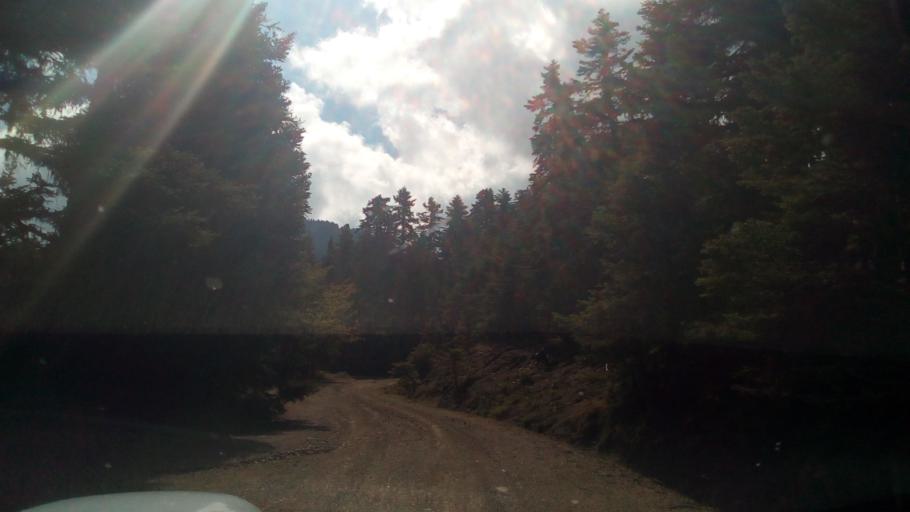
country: GR
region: Central Greece
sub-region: Nomos Fokidos
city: Lidoriki
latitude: 38.6405
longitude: 21.9492
